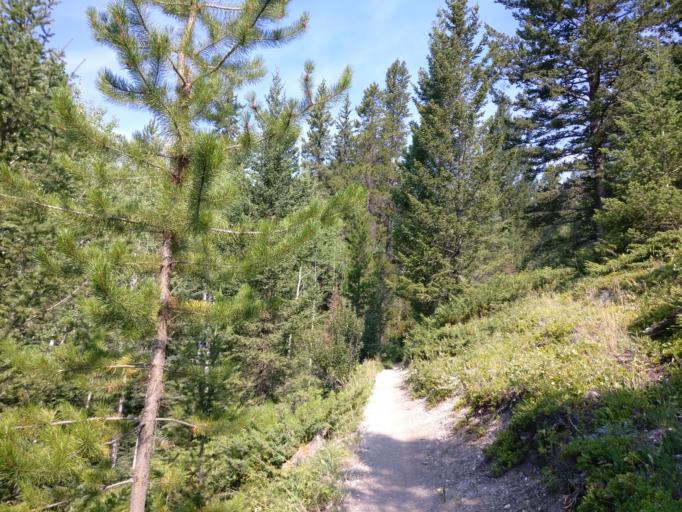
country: CA
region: Alberta
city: Canmore
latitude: 51.0825
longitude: -115.3195
